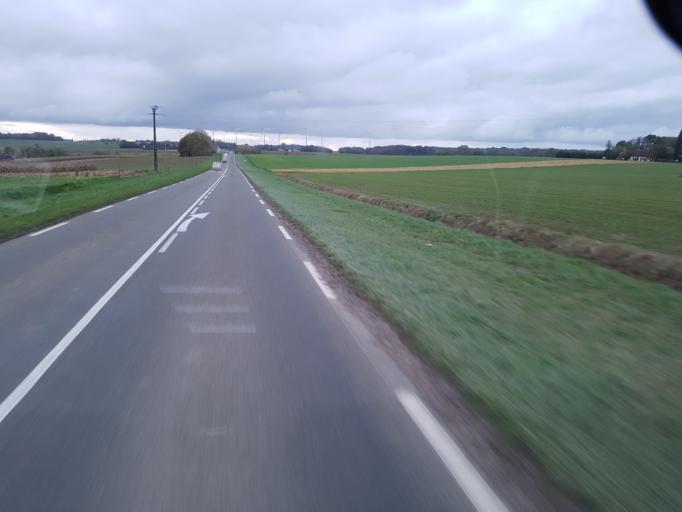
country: FR
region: Champagne-Ardenne
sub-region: Departement de la Marne
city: Montmirail
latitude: 48.8894
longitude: 3.4973
